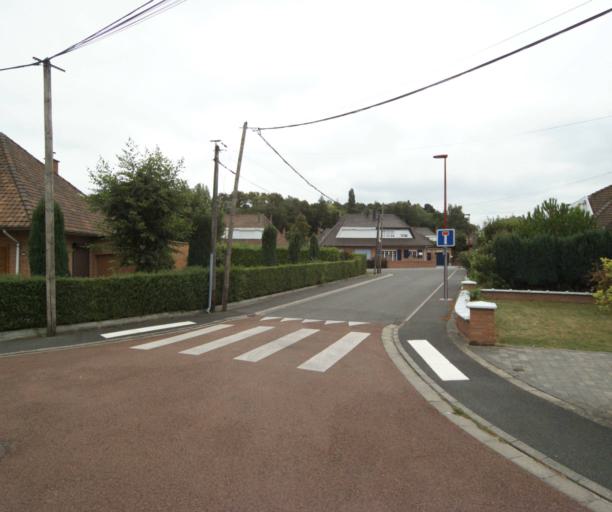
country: FR
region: Nord-Pas-de-Calais
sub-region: Departement du Nord
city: Leers
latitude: 50.6851
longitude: 3.2369
